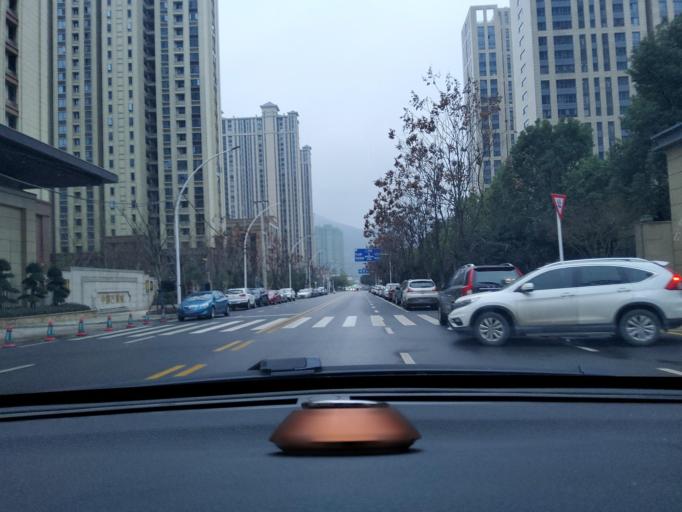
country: CN
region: Hubei
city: Tuanchengshan
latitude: 30.1974
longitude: 115.0094
